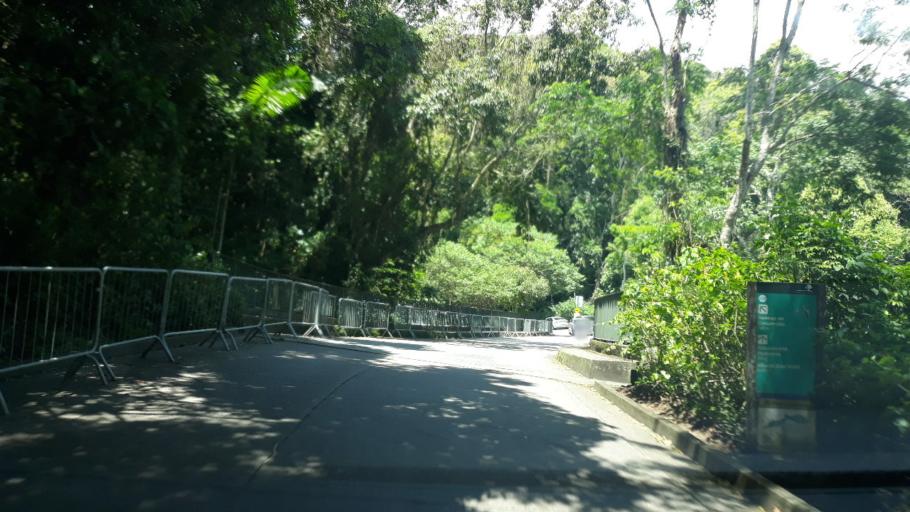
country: BR
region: Rio de Janeiro
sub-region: Rio De Janeiro
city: Rio de Janeiro
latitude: -22.9458
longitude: -43.2170
